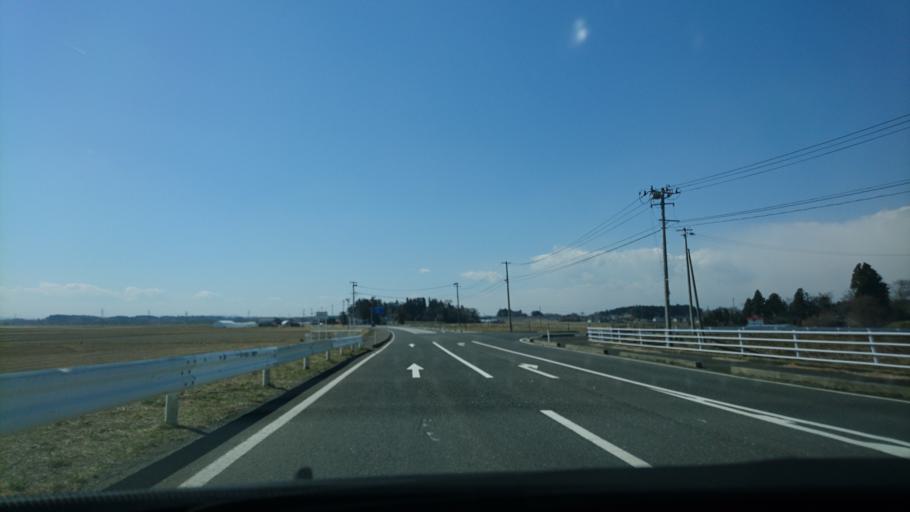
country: JP
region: Iwate
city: Ichinoseki
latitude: 38.7483
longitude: 141.1327
